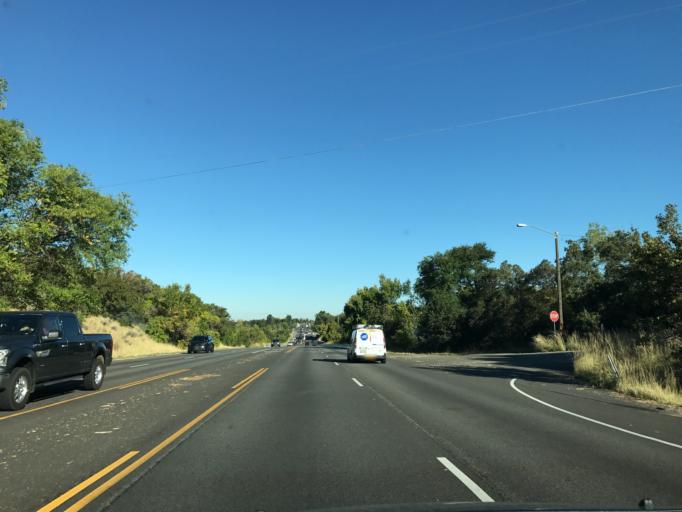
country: US
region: Utah
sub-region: Weber County
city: Uintah
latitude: 41.1647
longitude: -111.9422
